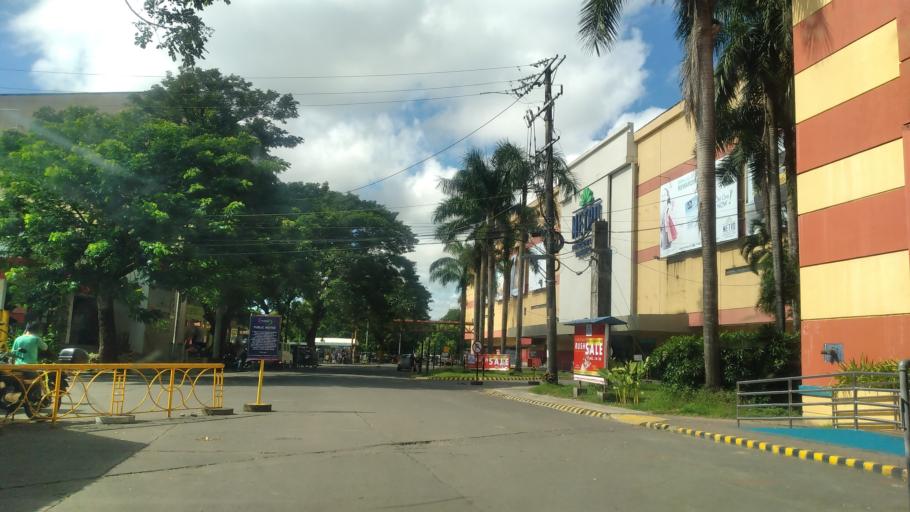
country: PH
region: Calabarzon
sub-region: Province of Quezon
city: Lucena
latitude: 13.9370
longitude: 121.6093
